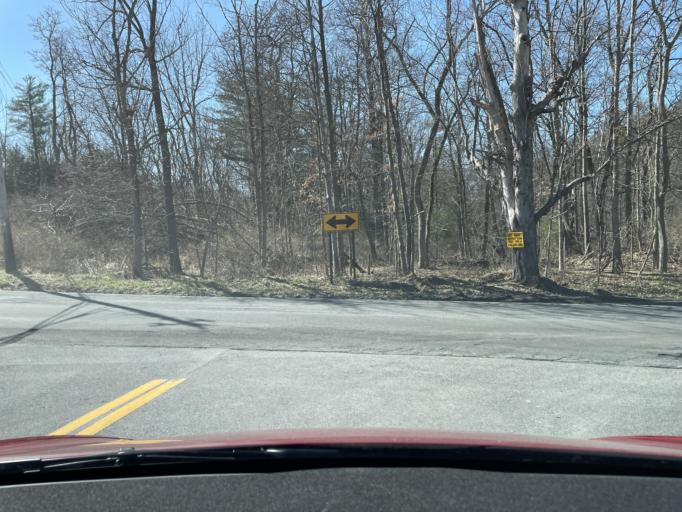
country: US
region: New York
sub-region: Ulster County
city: Zena
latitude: 42.0446
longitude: -74.0211
